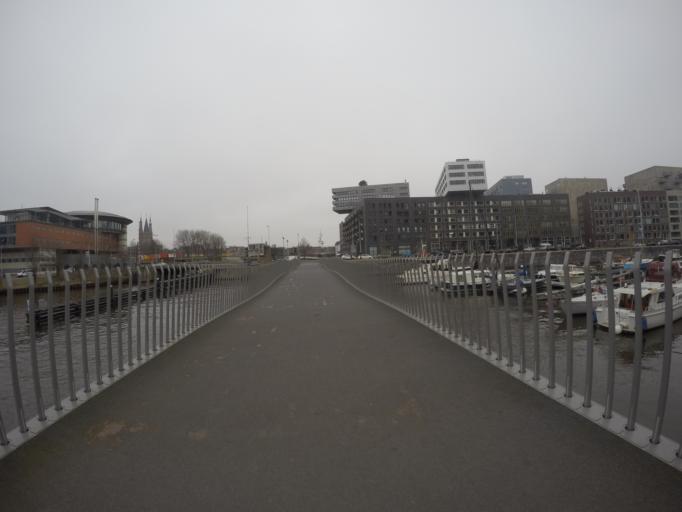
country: NL
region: North Holland
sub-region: Gemeente Amsterdam
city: Amsterdam
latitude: 52.3836
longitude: 4.8945
